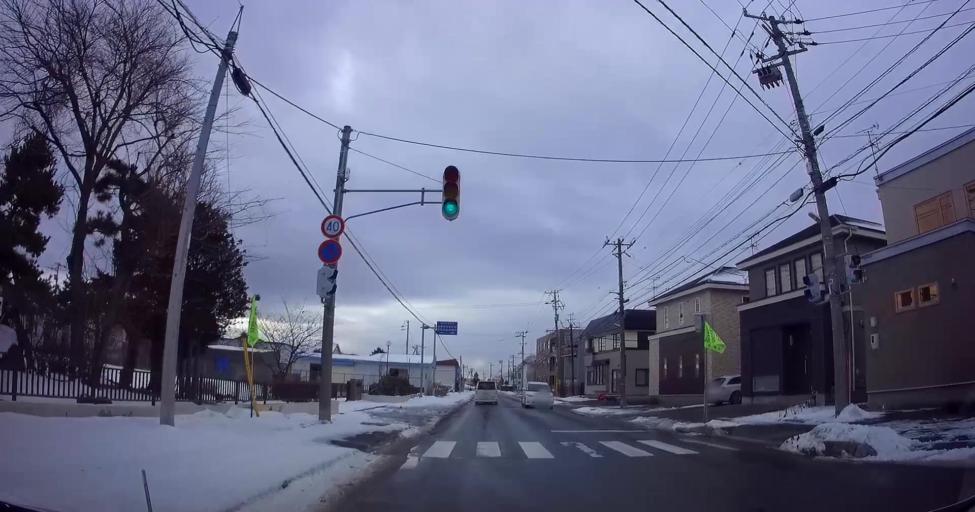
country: JP
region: Hokkaido
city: Kamiiso
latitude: 41.8283
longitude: 140.6866
